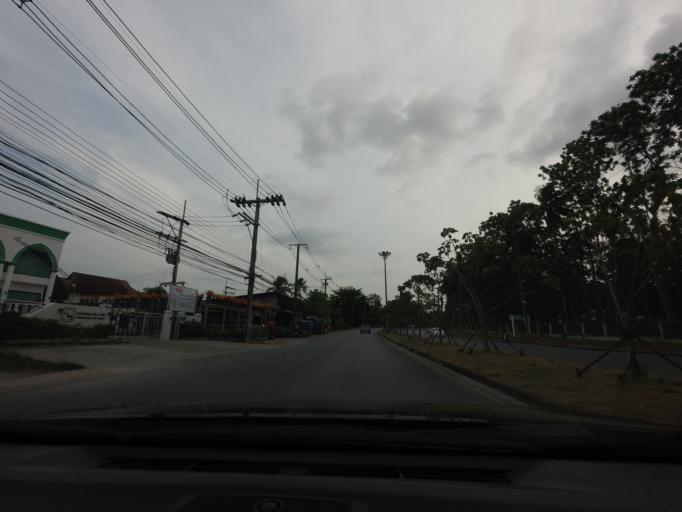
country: TH
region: Yala
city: Yala
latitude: 6.5236
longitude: 101.2823
